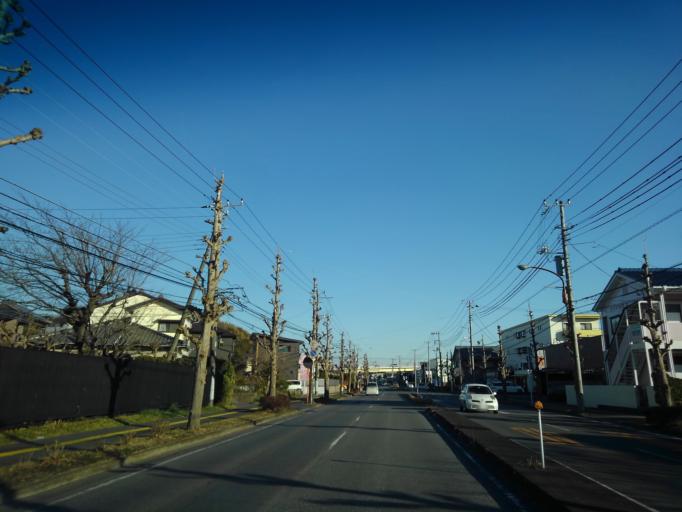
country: JP
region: Chiba
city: Kimitsu
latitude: 35.3332
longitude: 139.9005
